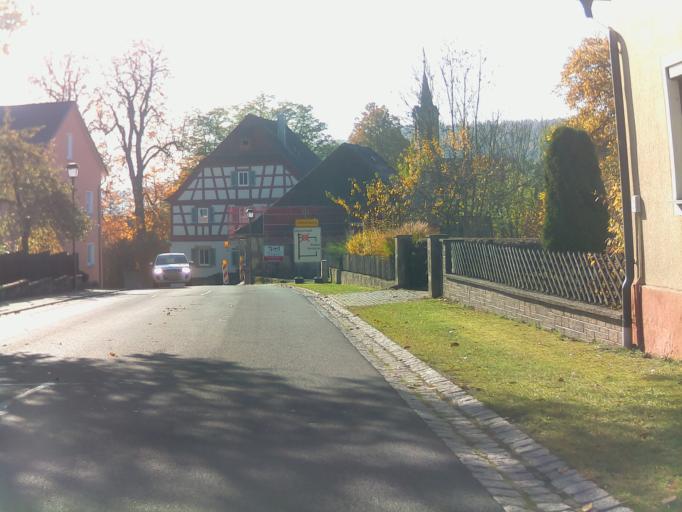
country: DE
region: Bavaria
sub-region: Regierungsbezirk Unterfranken
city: Knetzgau
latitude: 49.9249
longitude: 10.5563
